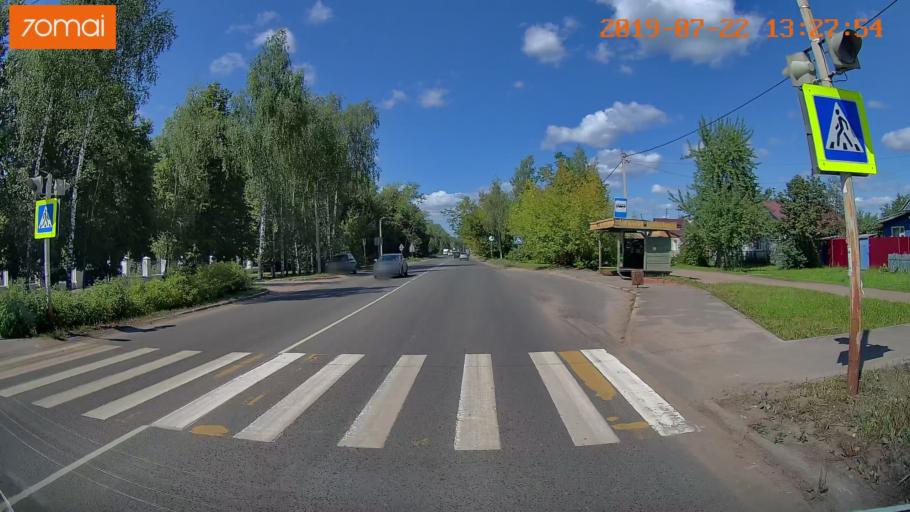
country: RU
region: Ivanovo
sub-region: Gorod Ivanovo
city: Ivanovo
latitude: 57.0386
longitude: 40.9501
